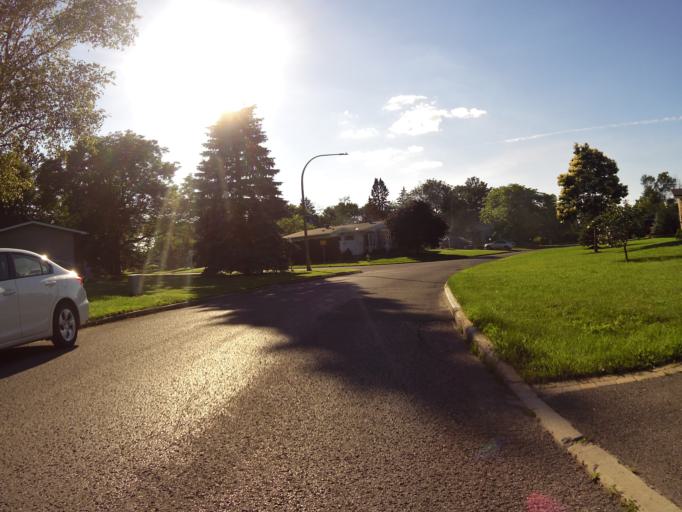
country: CA
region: Ontario
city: Bells Corners
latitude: 45.3396
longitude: -75.7489
